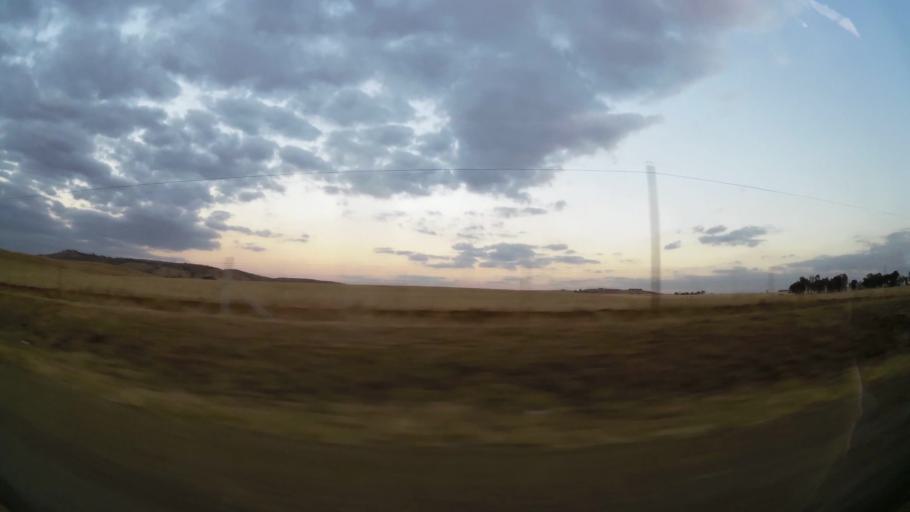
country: ZA
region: Gauteng
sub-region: West Rand District Municipality
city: Krugersdorp
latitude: -26.0558
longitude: 27.7063
